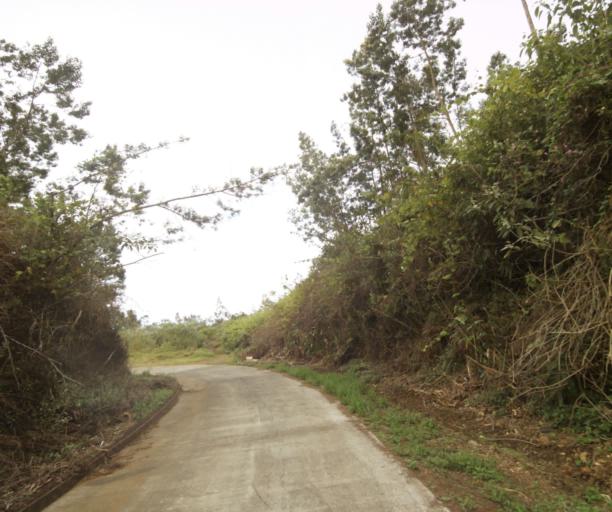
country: RE
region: Reunion
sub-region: Reunion
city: Saint-Paul
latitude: -21.0114
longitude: 55.3553
